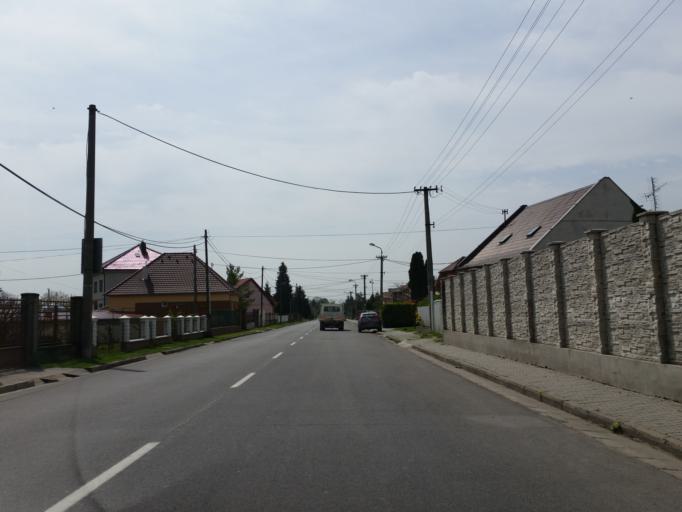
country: SK
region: Trnavsky
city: Leopoldov
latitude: 48.4332
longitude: 17.7680
